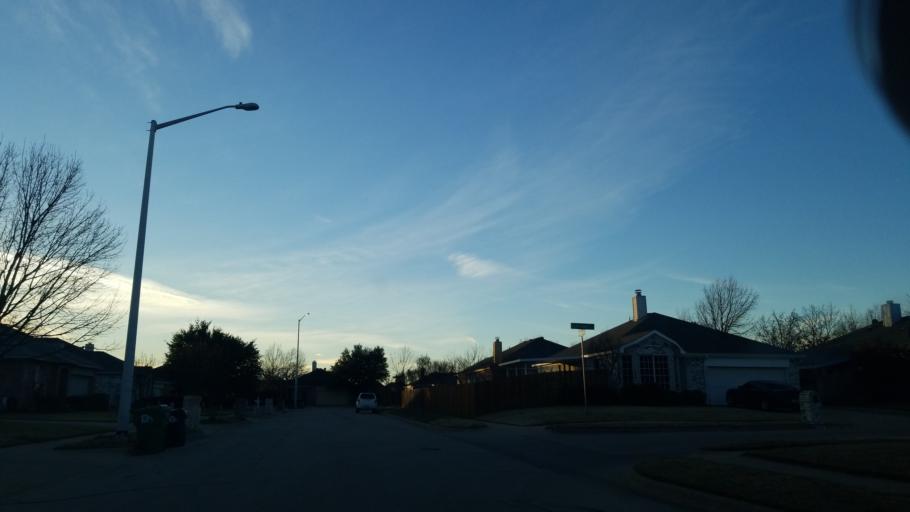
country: US
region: Texas
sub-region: Denton County
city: Corinth
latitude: 33.1589
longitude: -97.1086
